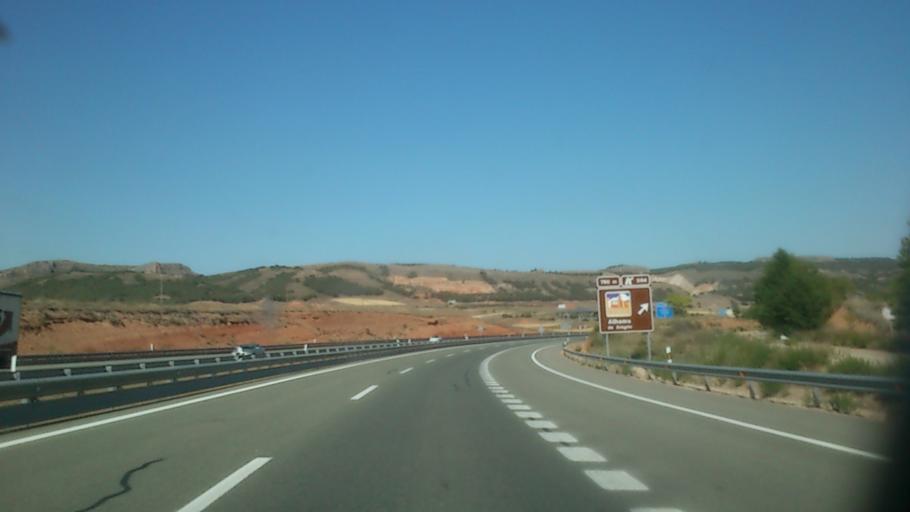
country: ES
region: Aragon
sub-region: Provincia de Zaragoza
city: Contamina
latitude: 41.3060
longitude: -1.9361
